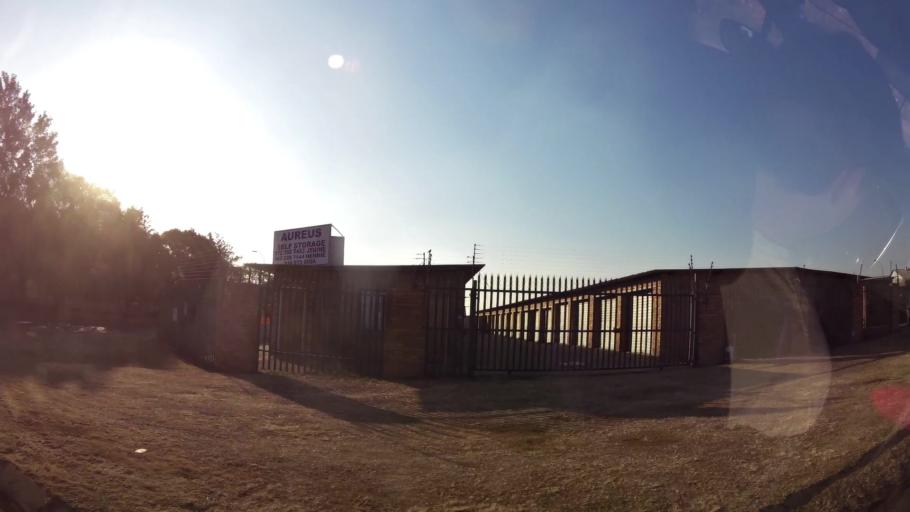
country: ZA
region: Gauteng
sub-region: West Rand District Municipality
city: Randfontein
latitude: -26.2013
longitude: 27.6885
